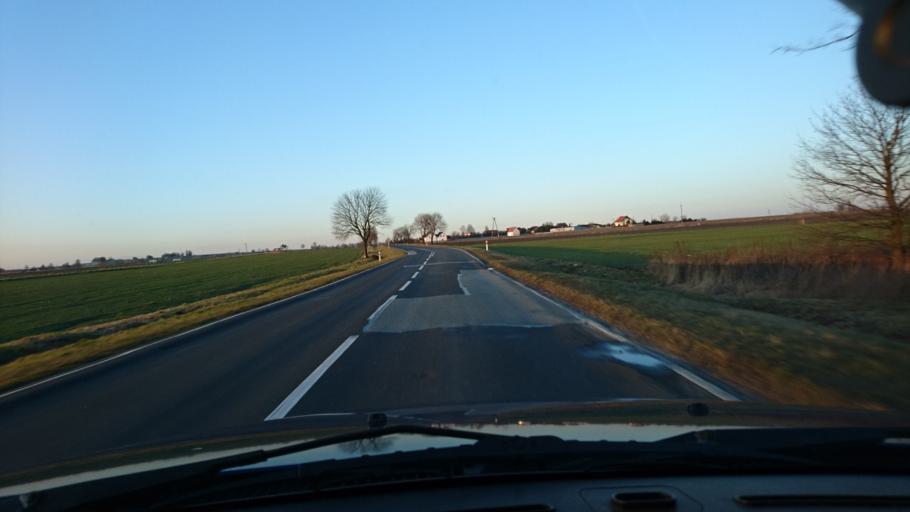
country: PL
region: Silesian Voivodeship
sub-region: Powiat gliwicki
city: Wielowies
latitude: 50.4649
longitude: 18.6110
